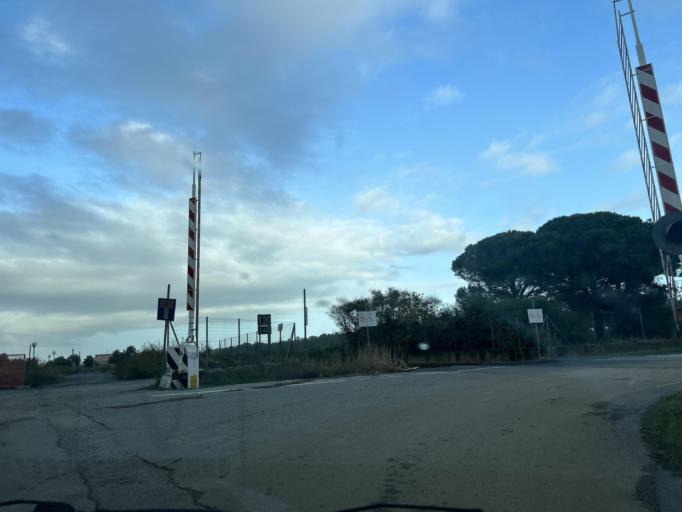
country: IT
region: Calabria
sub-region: Provincia di Catanzaro
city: Squillace Lido
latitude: 38.7794
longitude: 16.5726
